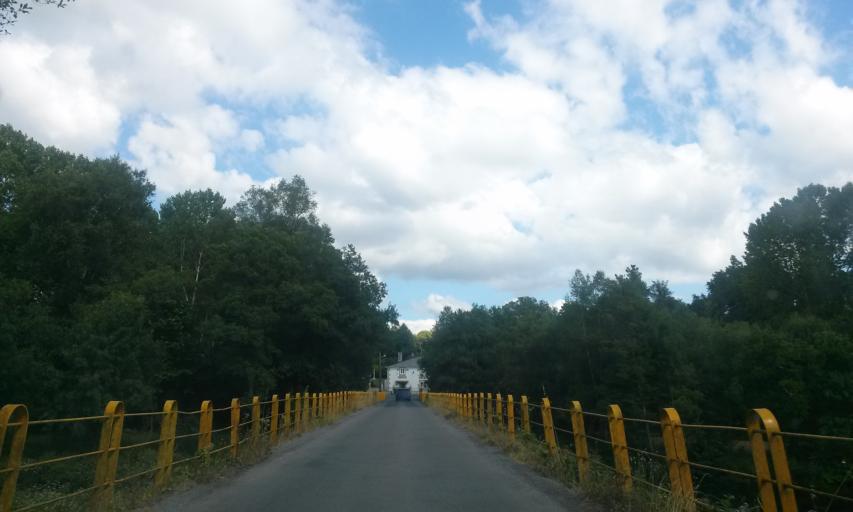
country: ES
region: Galicia
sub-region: Provincia de Lugo
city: Rabade
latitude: 43.1165
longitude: -7.6574
